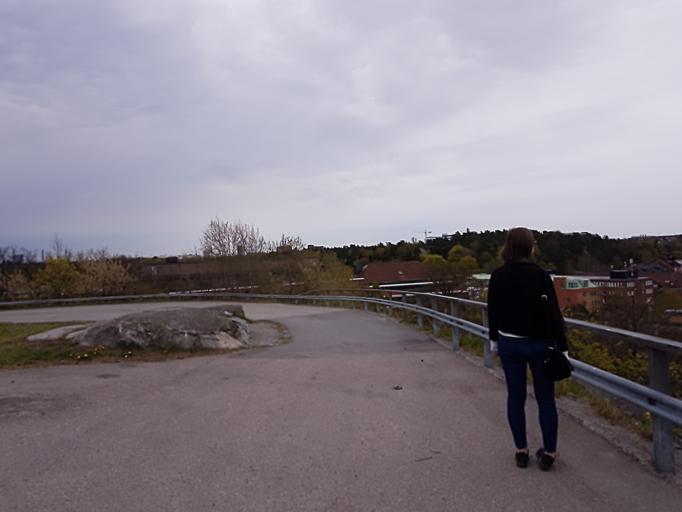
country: SE
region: Stockholm
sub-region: Solna Kommun
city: Solna
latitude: 59.3597
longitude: 18.0141
